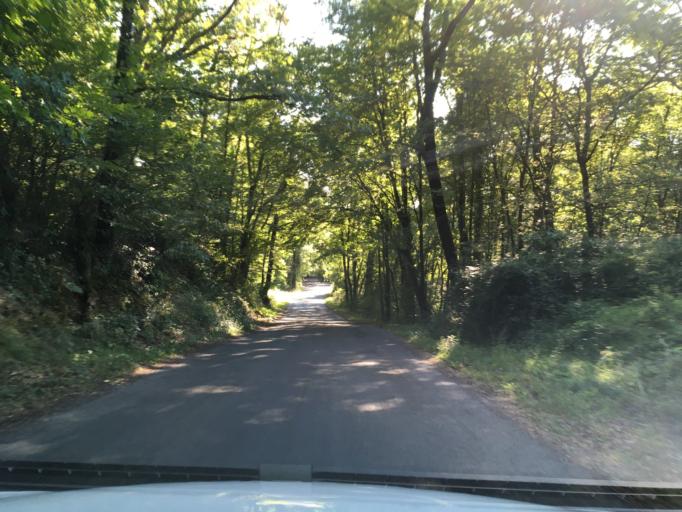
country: FR
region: Limousin
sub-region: Departement de la Correze
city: Malemort-sur-Correze
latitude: 45.1773
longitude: 1.5385
